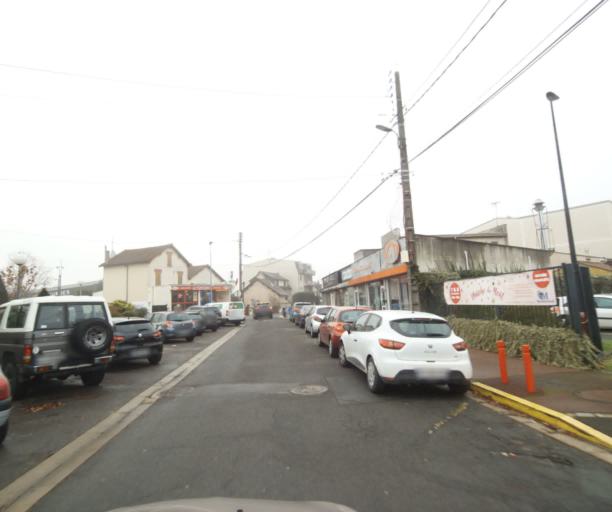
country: FR
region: Ile-de-France
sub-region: Departement de Seine-Saint-Denis
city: Montfermeil
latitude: 48.9051
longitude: 2.5853
